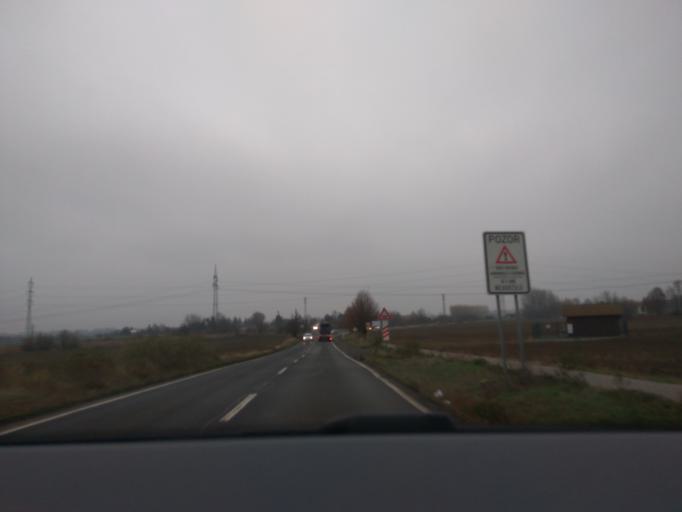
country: CZ
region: Central Bohemia
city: Hovorcovice
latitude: 50.1716
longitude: 14.5206
